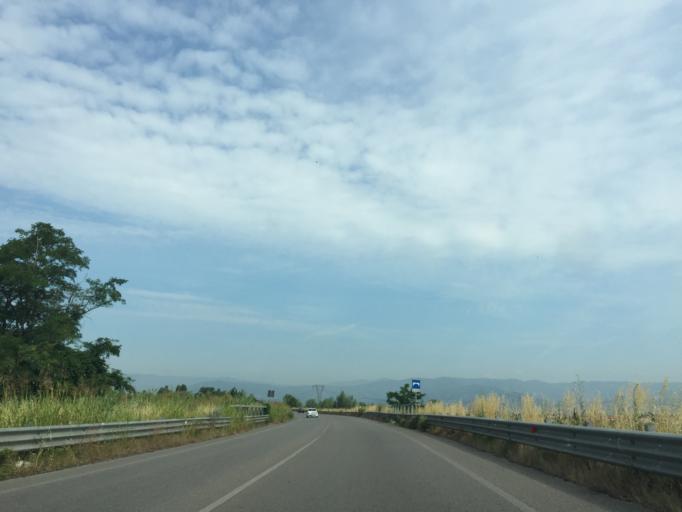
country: IT
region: Tuscany
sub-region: Provincia di Pistoia
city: Uggia-Pazzera-Bizzarrino
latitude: 43.8353
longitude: 10.8261
